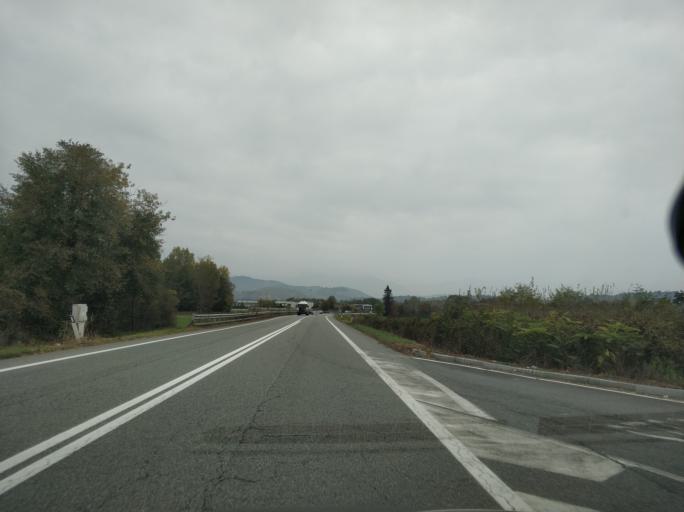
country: IT
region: Piedmont
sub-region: Provincia di Torino
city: Bairo
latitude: 45.3803
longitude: 7.7331
